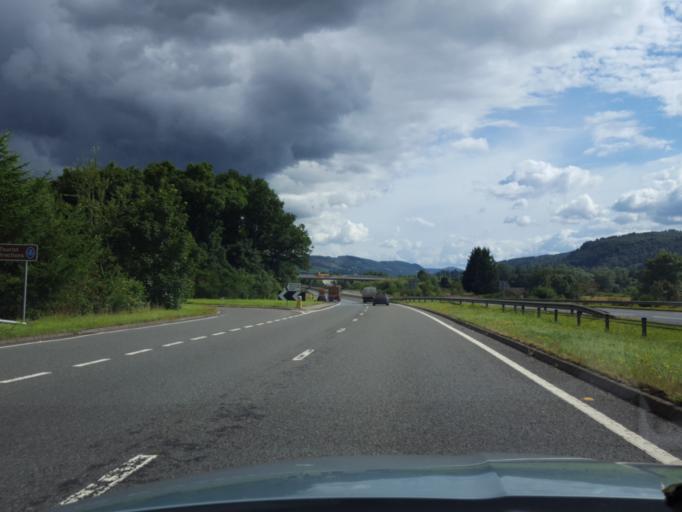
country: GB
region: Scotland
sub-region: Perth and Kinross
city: Pitlochry
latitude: 56.6543
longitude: -3.6711
